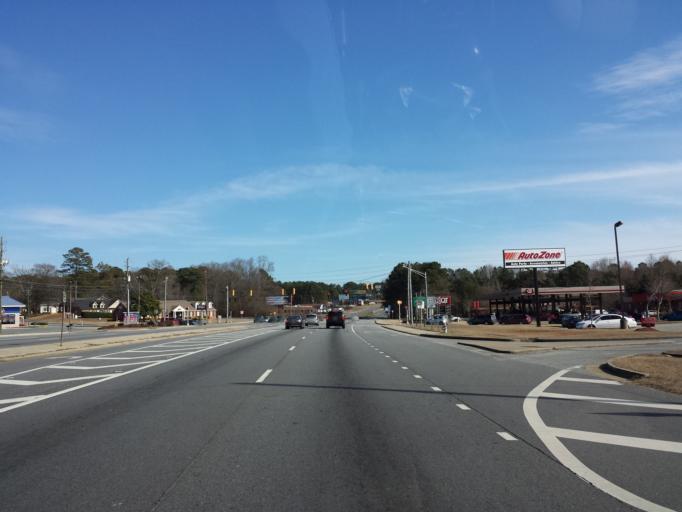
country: US
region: Georgia
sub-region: Cobb County
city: Kennesaw
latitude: 34.0209
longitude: -84.6230
